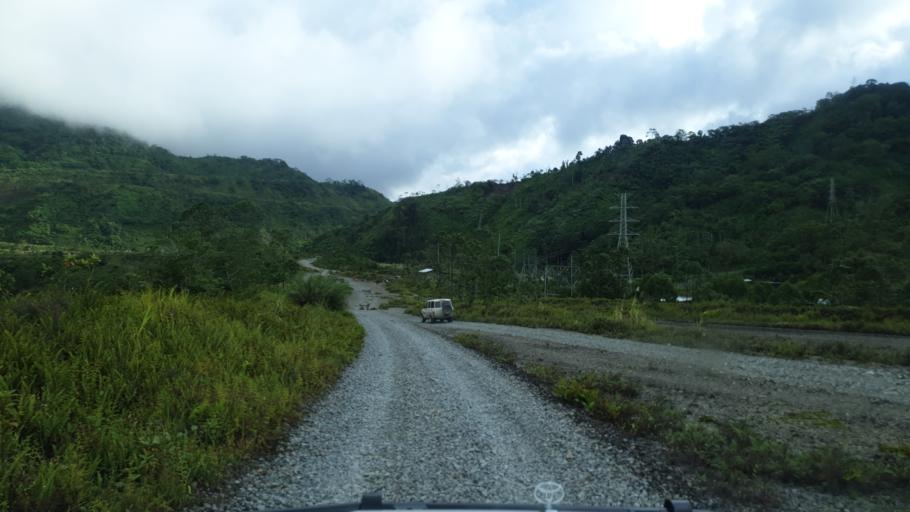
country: PG
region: Bougainville
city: Panguna
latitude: -6.3099
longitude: 155.4880
